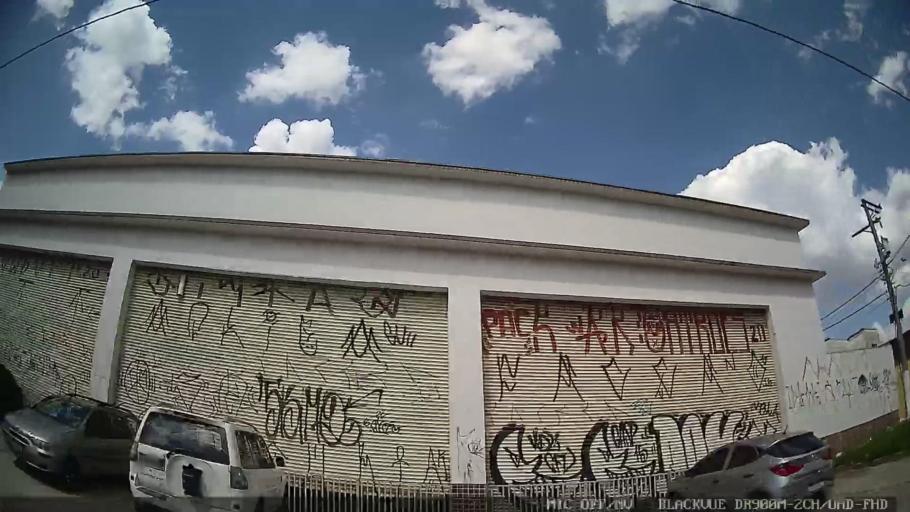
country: BR
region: Sao Paulo
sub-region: Guarulhos
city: Guarulhos
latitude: -23.5347
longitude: -46.4860
